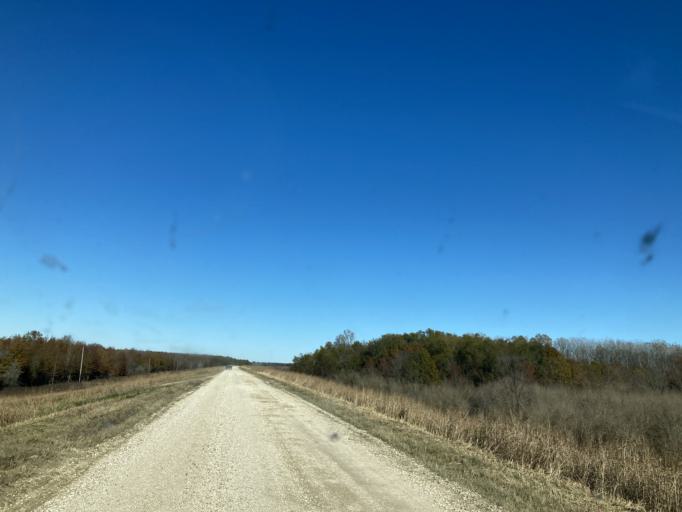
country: US
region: Mississippi
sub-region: Sharkey County
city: Rolling Fork
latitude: 32.7523
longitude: -90.6596
